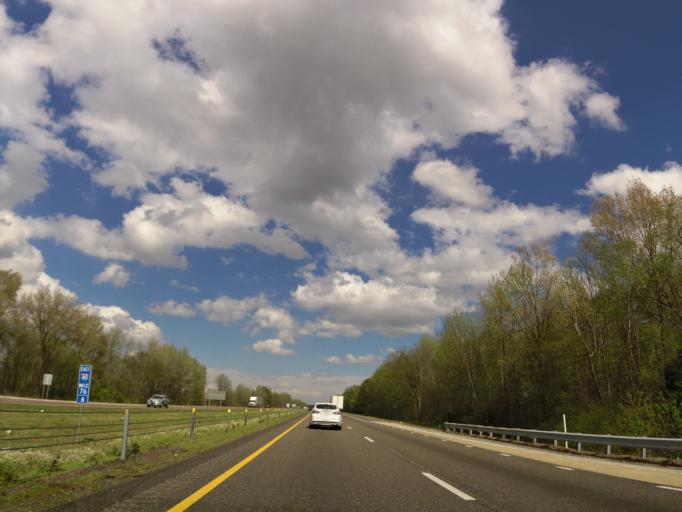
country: US
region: Tennessee
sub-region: Madison County
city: Jackson
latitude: 35.6426
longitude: -88.9162
